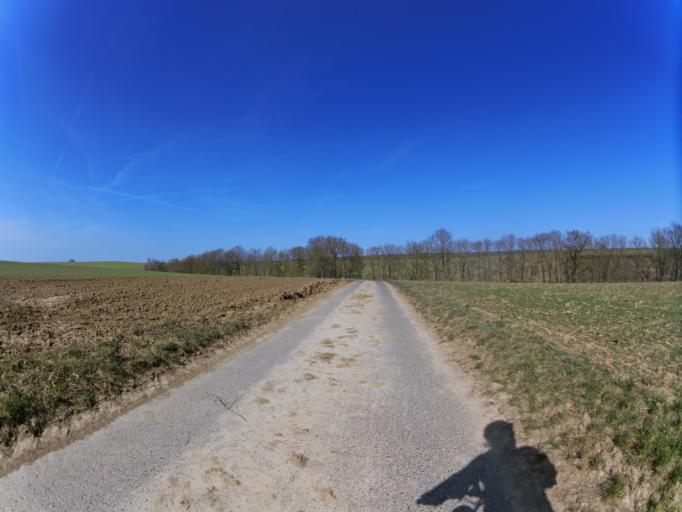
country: DE
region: Bavaria
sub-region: Regierungsbezirk Unterfranken
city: Dettelbach
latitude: 49.8233
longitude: 10.1424
